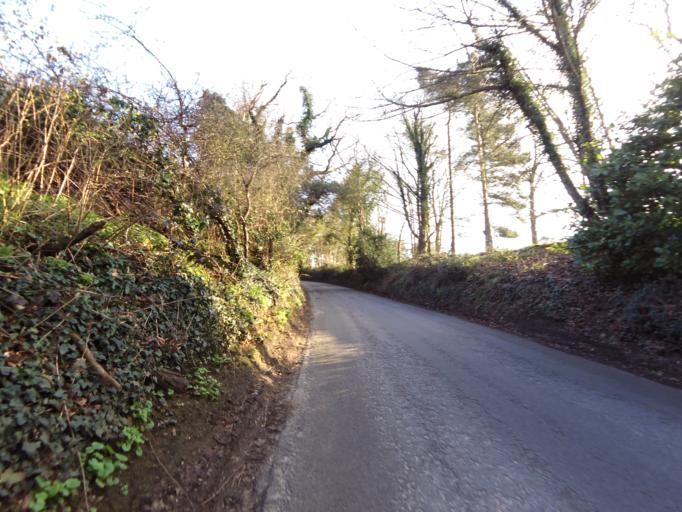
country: GB
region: England
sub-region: Suffolk
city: Kesgrave
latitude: 52.0784
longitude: 1.2533
